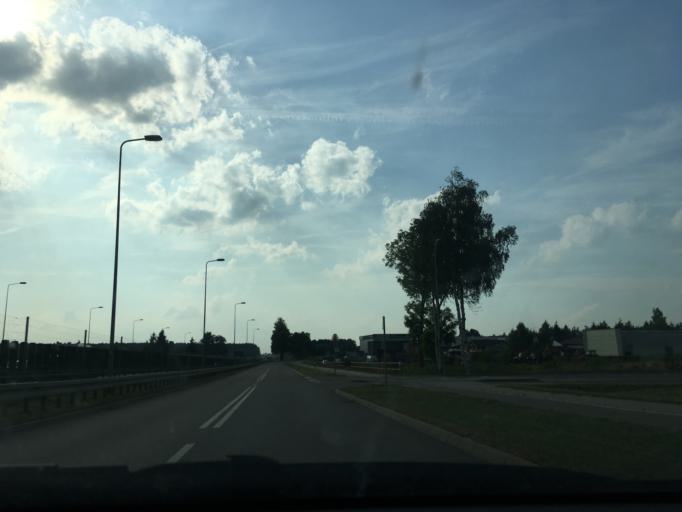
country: PL
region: Podlasie
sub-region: Powiat bialostocki
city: Choroszcz
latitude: 53.1517
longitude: 23.0419
